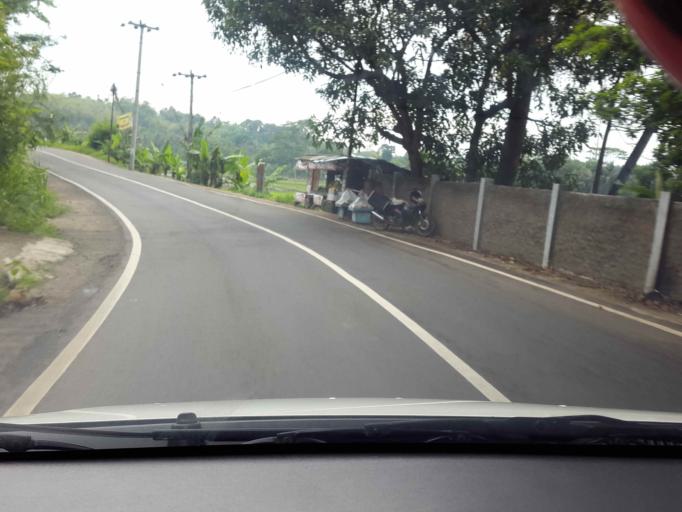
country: ID
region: West Java
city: Cidadap
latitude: -7.0213
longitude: 106.5629
